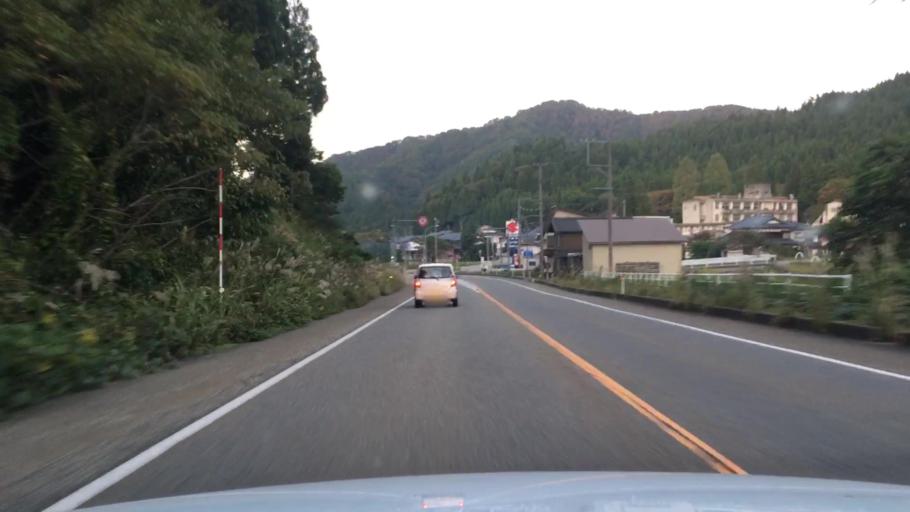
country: JP
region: Niigata
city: Murakami
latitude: 38.4357
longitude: 139.5898
